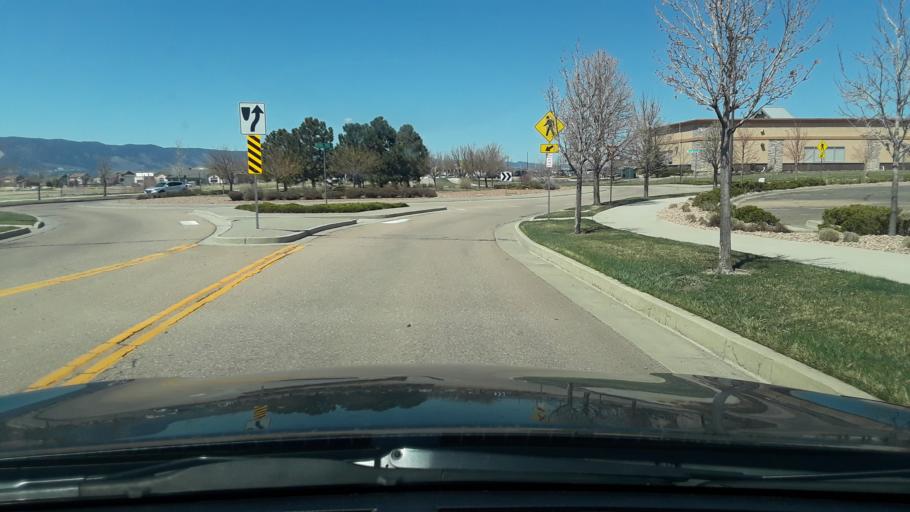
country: US
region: Colorado
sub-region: El Paso County
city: Black Forest
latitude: 38.9686
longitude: -104.7479
